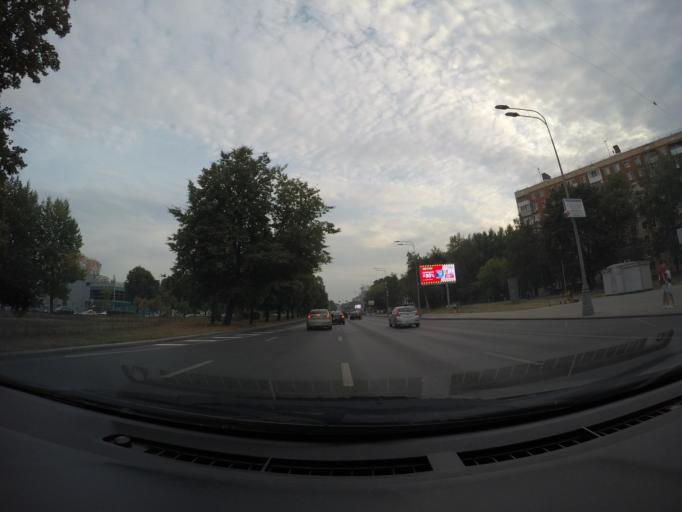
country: RU
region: Moskovskaya
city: Kozhukhovo
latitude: 55.6794
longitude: 37.6637
